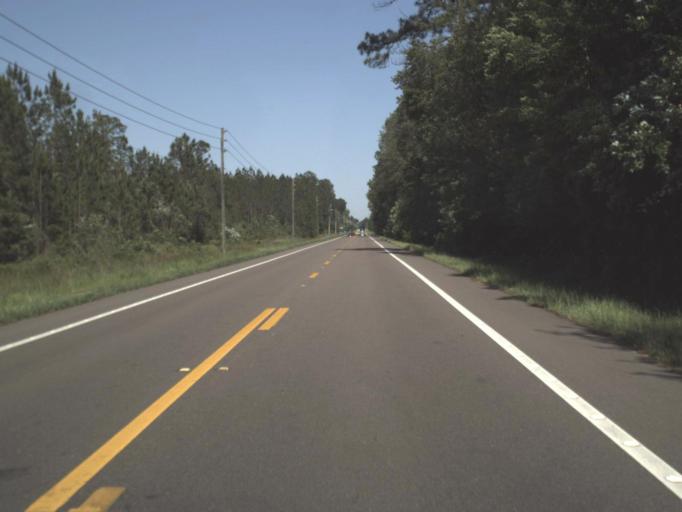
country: US
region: Florida
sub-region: Duval County
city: Baldwin
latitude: 30.3028
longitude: -82.0203
